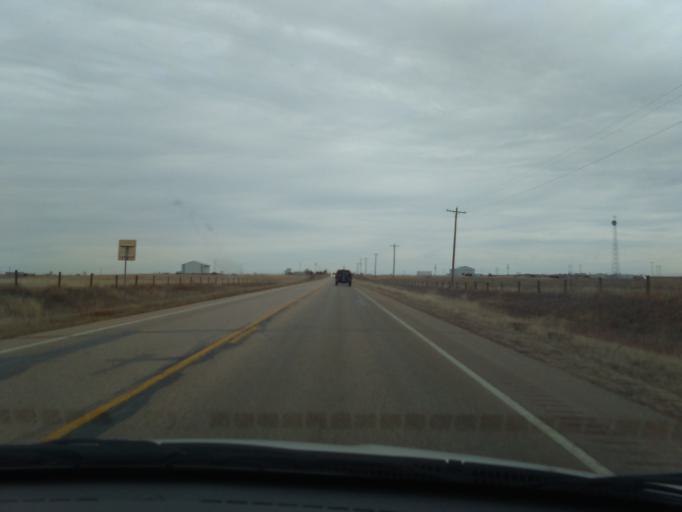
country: US
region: Colorado
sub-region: Yuma County
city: Yuma
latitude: 40.1490
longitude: -102.9517
